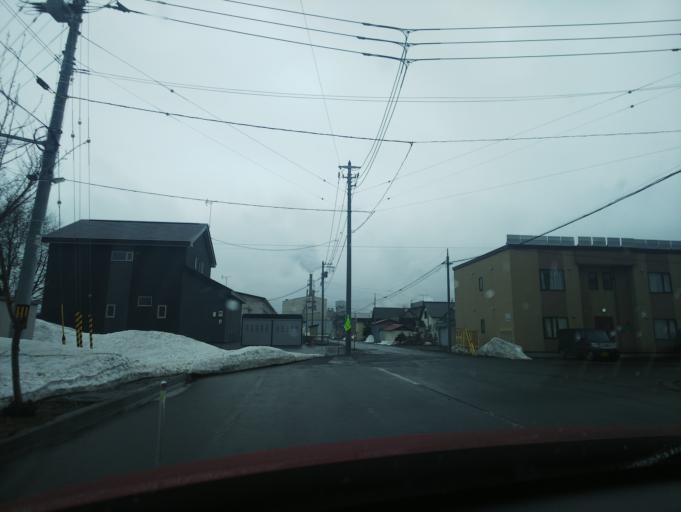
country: JP
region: Hokkaido
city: Nayoro
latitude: 44.3432
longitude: 142.4605
